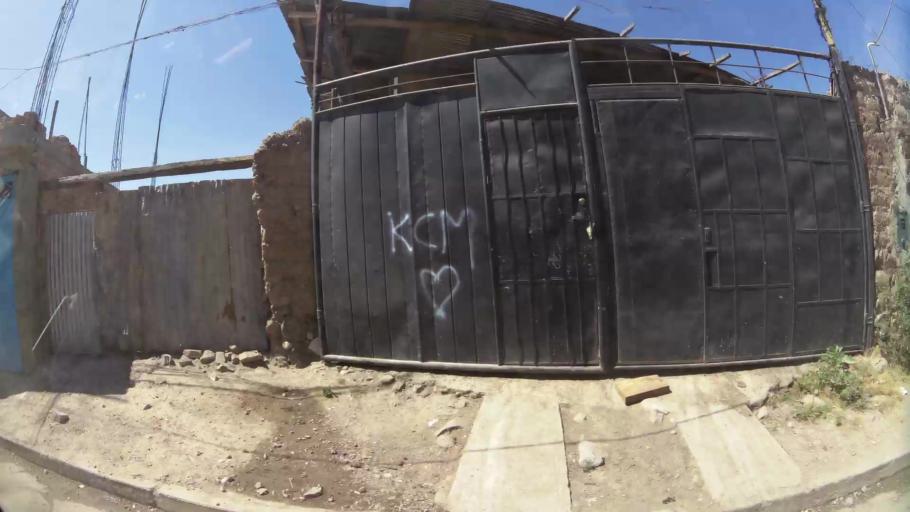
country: PE
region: Ayacucho
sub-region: Provincia de Huamanga
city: Ayacucho
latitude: -13.1599
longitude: -74.2367
